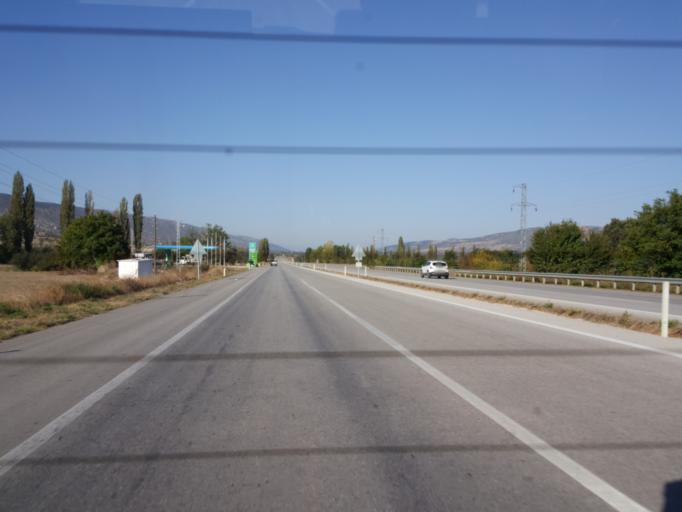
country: TR
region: Amasya
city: Ezinepazari
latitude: 40.5709
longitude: 36.0994
